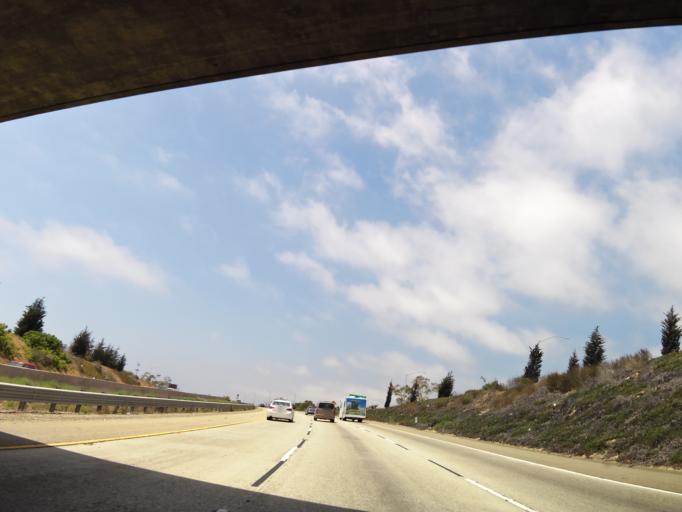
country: US
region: California
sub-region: Santa Barbara County
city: Carpinteria
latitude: 34.3838
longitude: -119.4844
